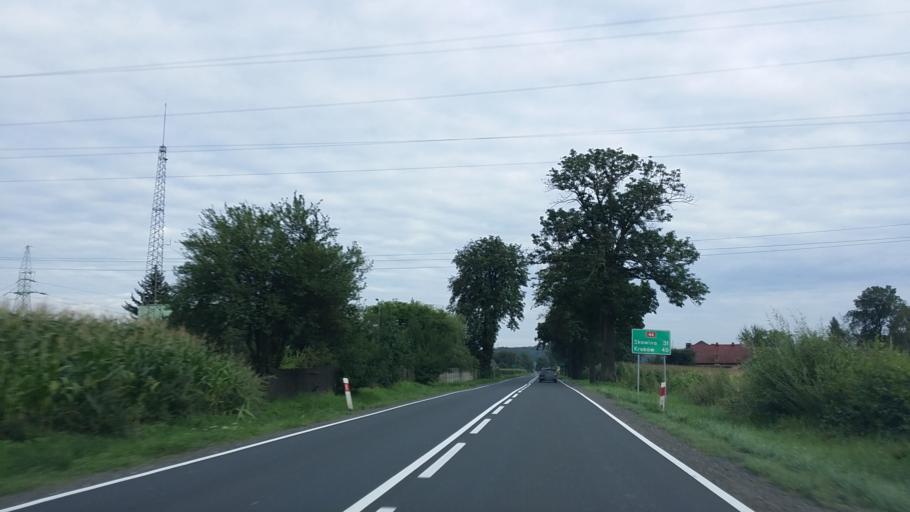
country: PL
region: Lesser Poland Voivodeship
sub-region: Powiat oswiecimski
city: Zator
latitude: 49.9987
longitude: 19.4527
